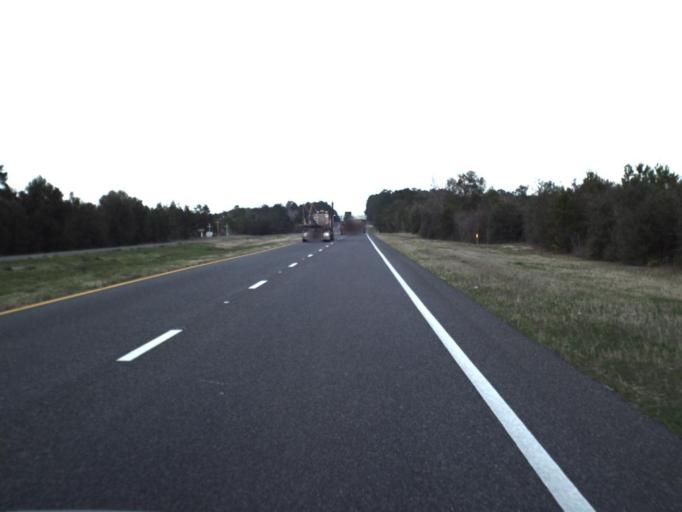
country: US
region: Florida
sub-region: Bay County
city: Youngstown
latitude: 30.5454
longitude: -85.3912
